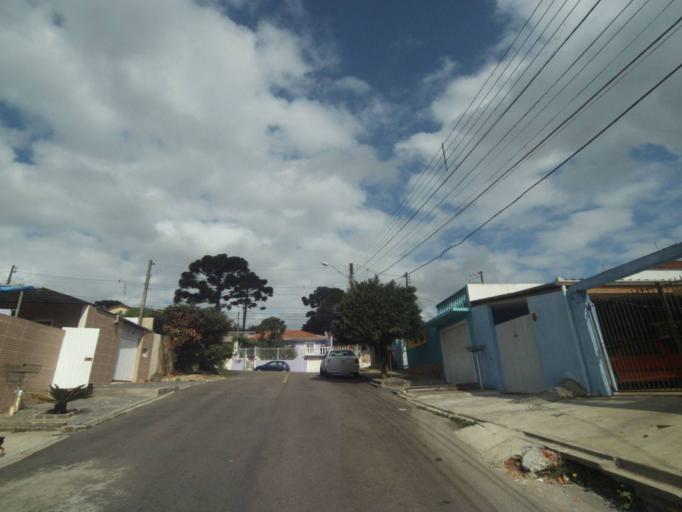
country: BR
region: Parana
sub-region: Curitiba
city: Curitiba
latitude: -25.3811
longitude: -49.3000
